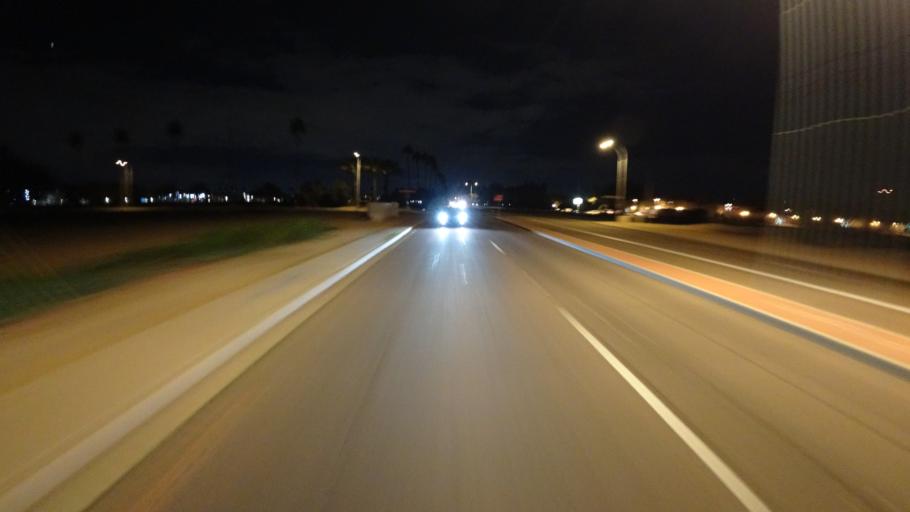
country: US
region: Arizona
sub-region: Maricopa County
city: Guadalupe
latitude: 33.3121
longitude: -111.9632
